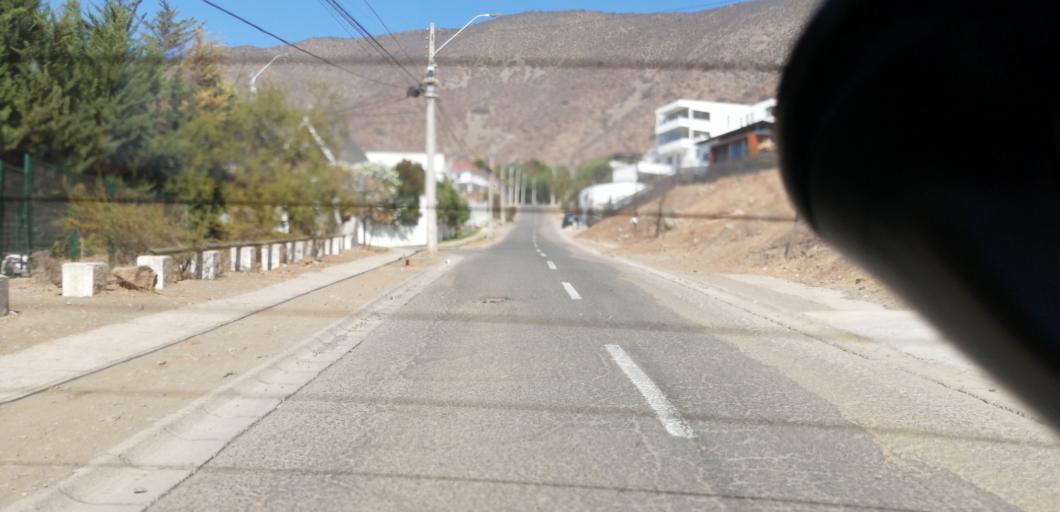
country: CL
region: Santiago Metropolitan
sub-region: Provincia de Santiago
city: Lo Prado
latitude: -33.4535
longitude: -70.8247
